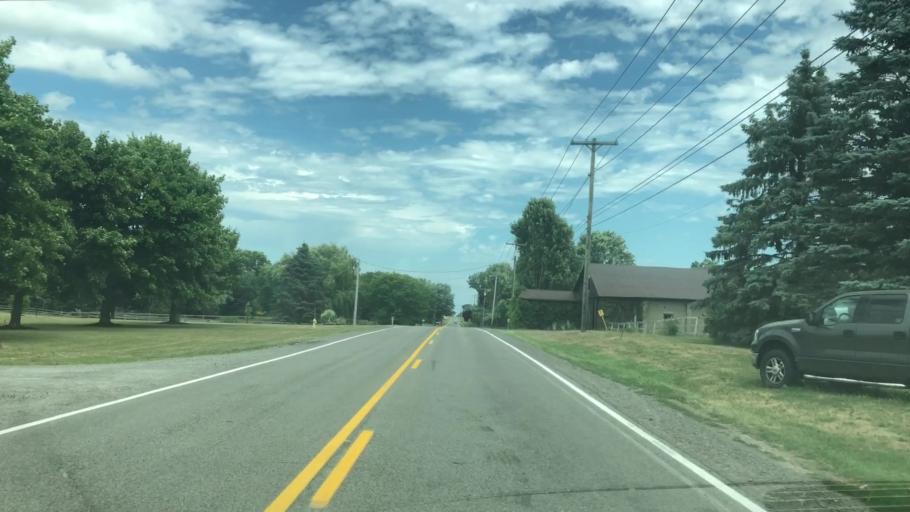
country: US
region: New York
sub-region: Monroe County
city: Webster
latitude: 43.1623
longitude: -77.4005
